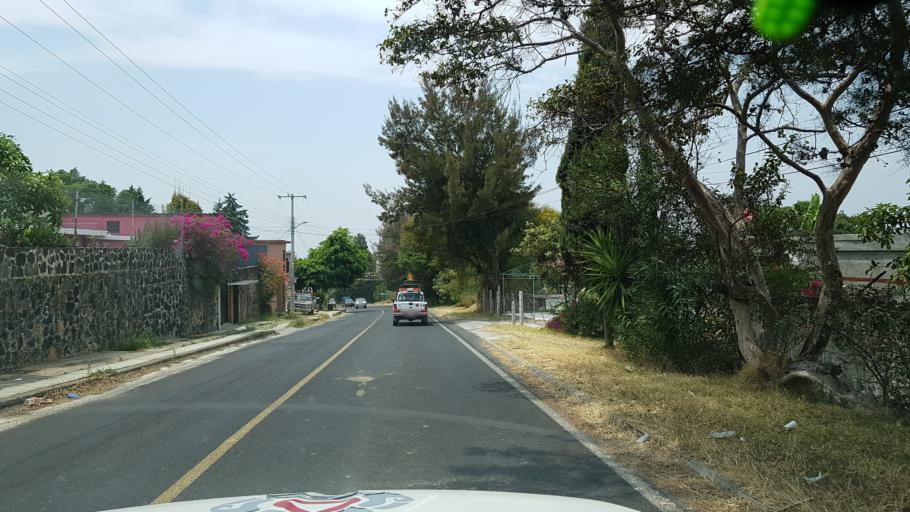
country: MX
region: Morelos
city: Ocuituco
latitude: 18.8819
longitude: -98.7687
